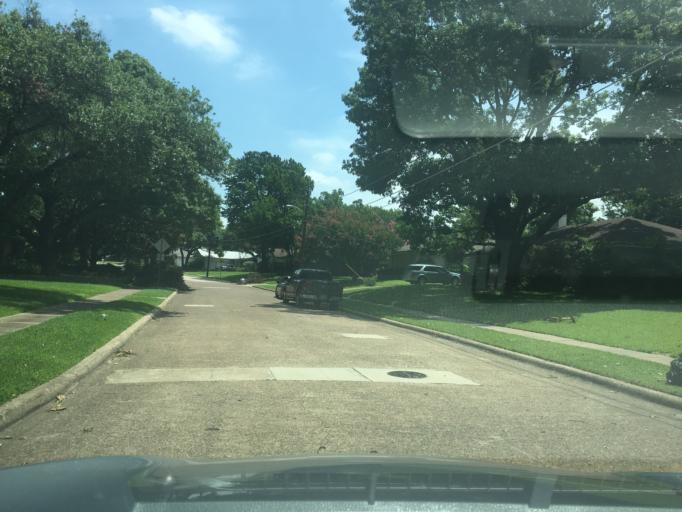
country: US
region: Texas
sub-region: Dallas County
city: Richardson
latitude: 32.9420
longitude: -96.7548
